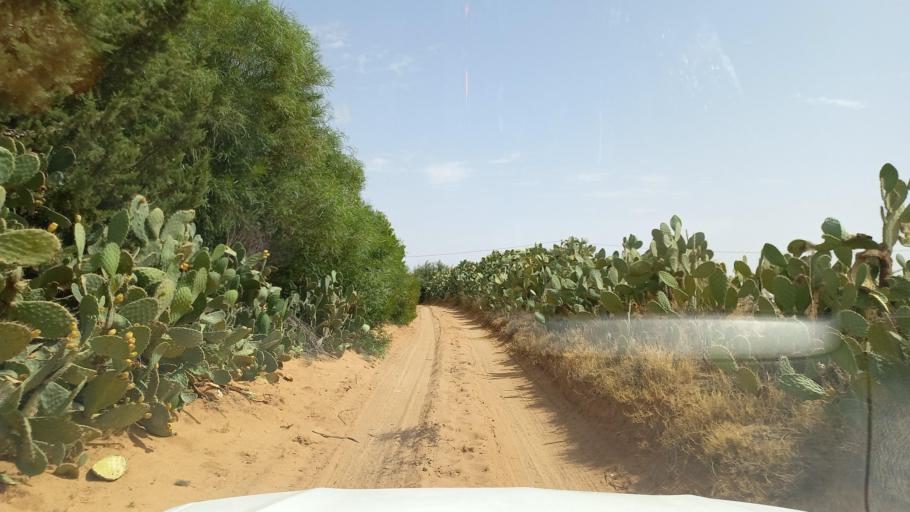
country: TN
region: Al Qasrayn
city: Kasserine
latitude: 35.2493
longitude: 9.0617
